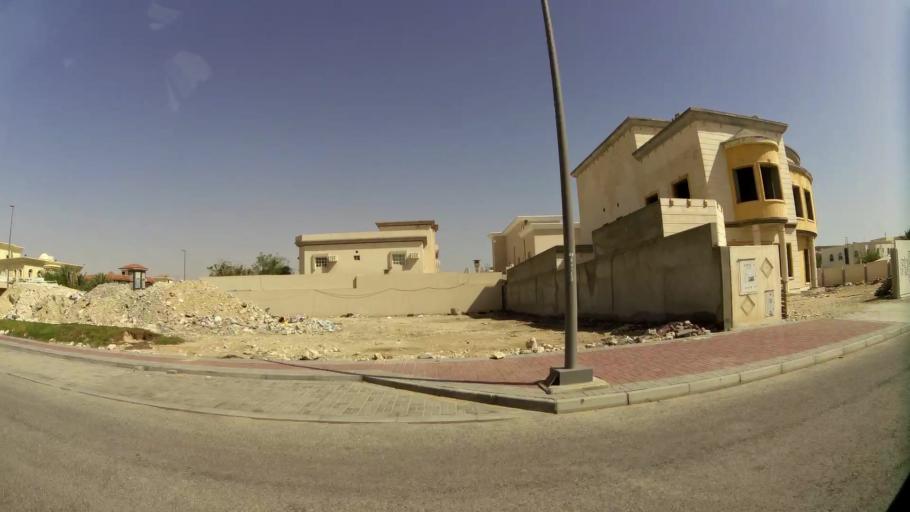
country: QA
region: Baladiyat ad Dawhah
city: Doha
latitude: 25.3529
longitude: 51.5056
